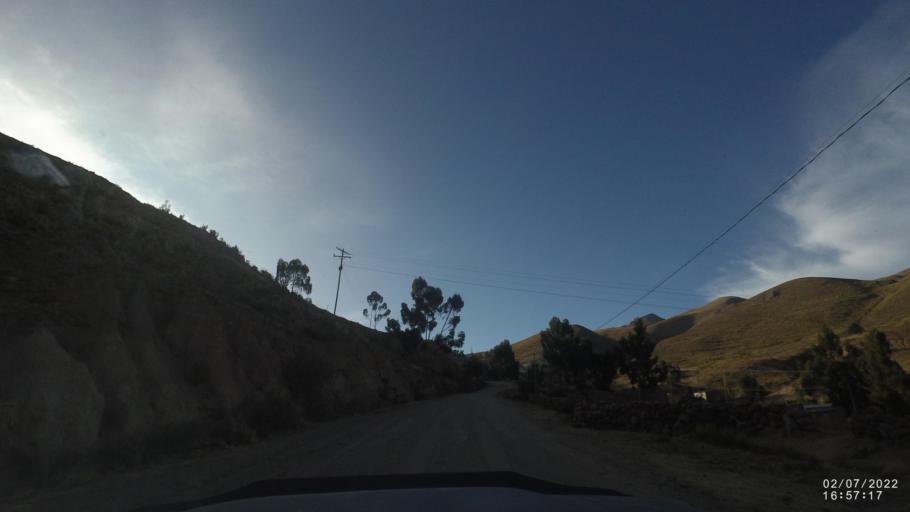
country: BO
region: Cochabamba
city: Irpa Irpa
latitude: -17.9502
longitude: -66.5458
